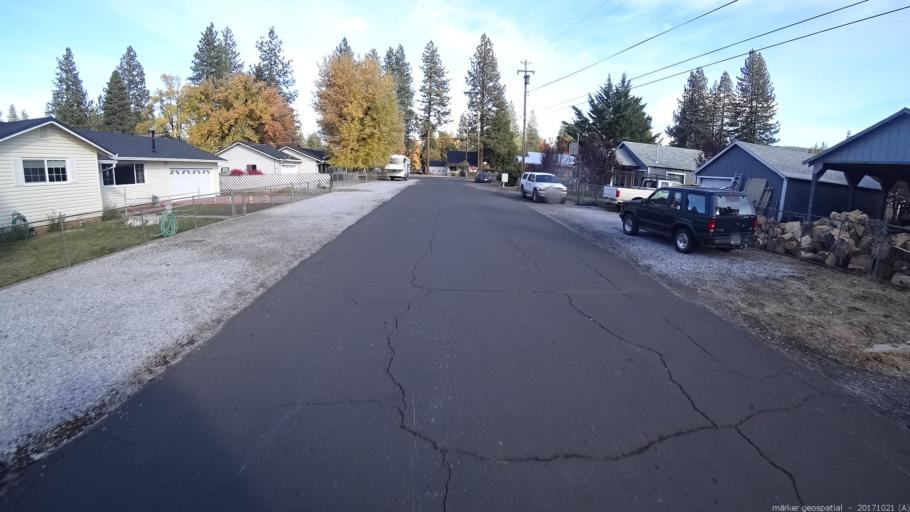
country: US
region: California
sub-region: Shasta County
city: Burney
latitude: 40.8790
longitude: -121.6636
